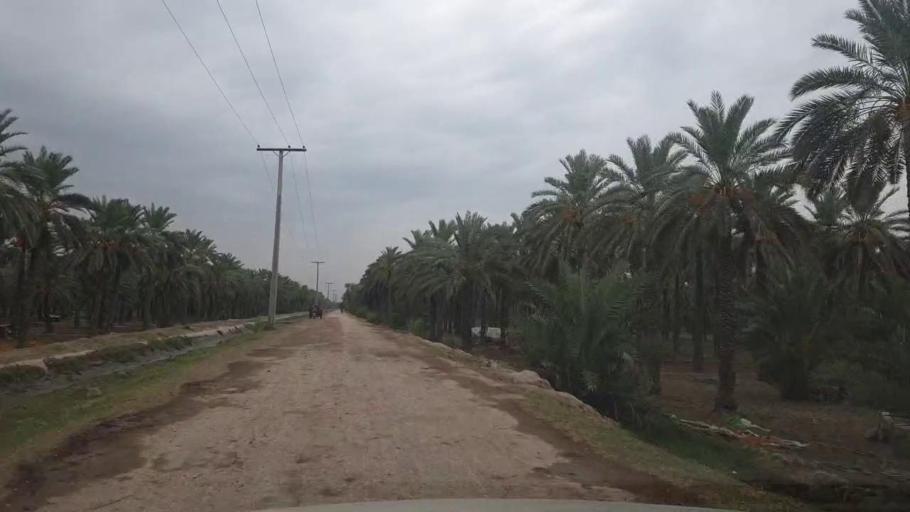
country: PK
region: Sindh
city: Khairpur
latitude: 27.6098
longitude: 68.8171
